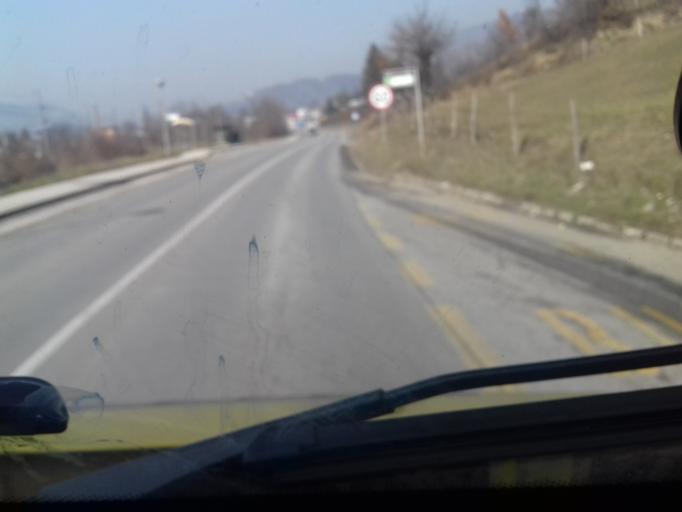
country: BA
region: Federation of Bosnia and Herzegovina
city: Vogosca
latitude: 43.9120
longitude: 18.3233
